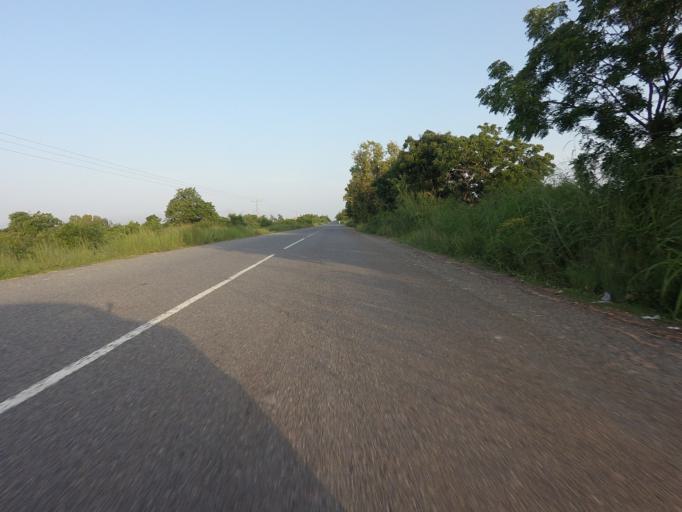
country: GH
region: Volta
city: Anloga
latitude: 5.8606
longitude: 0.7640
